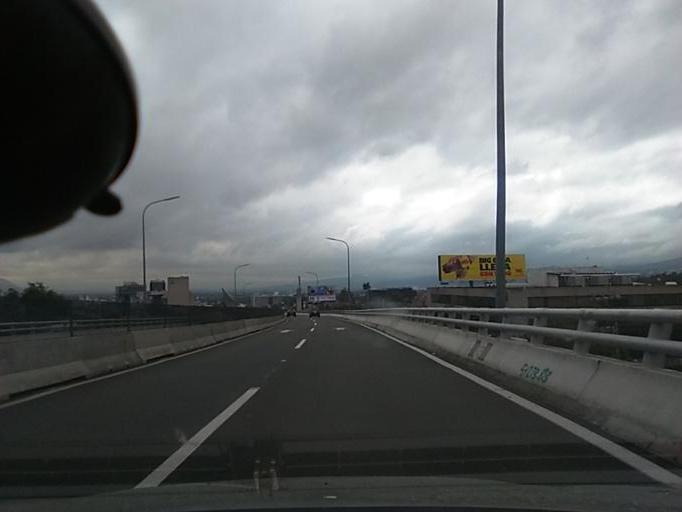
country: MX
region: Mexico City
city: Tlalpan
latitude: 19.3027
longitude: -99.1976
